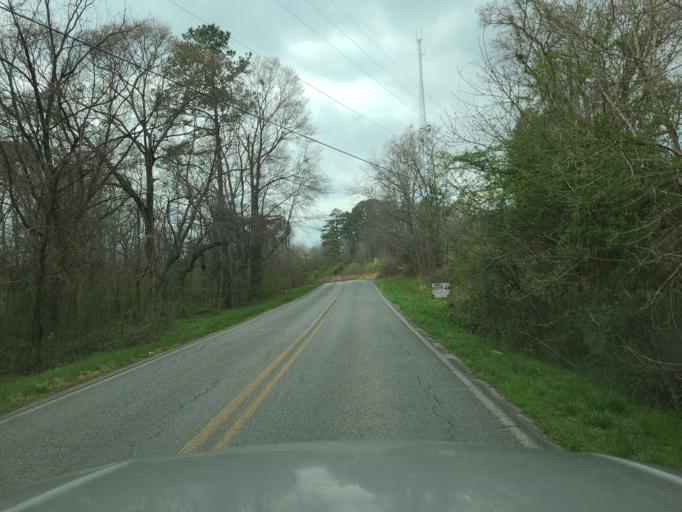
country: US
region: North Carolina
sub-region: Cleveland County
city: Boiling Springs
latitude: 35.2565
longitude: -81.6889
